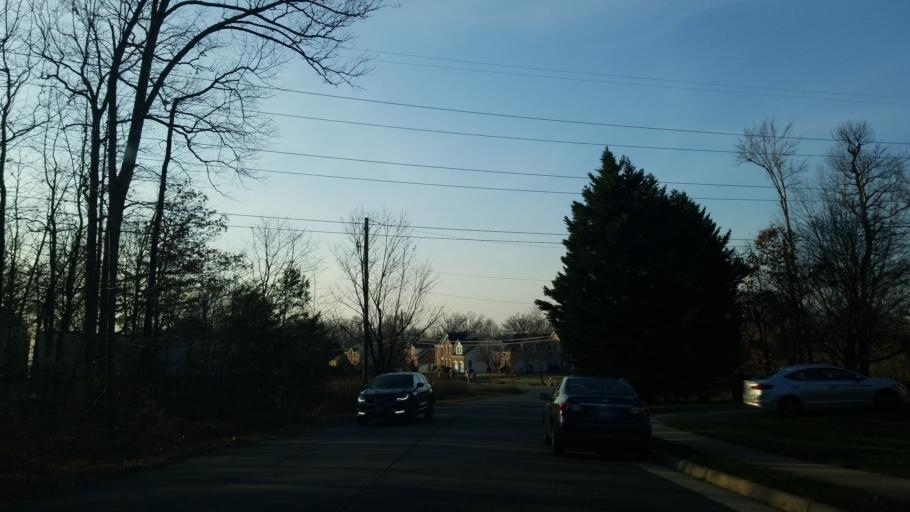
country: US
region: Virginia
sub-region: Fairfax County
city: Greenbriar
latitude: 38.8503
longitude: -77.3993
